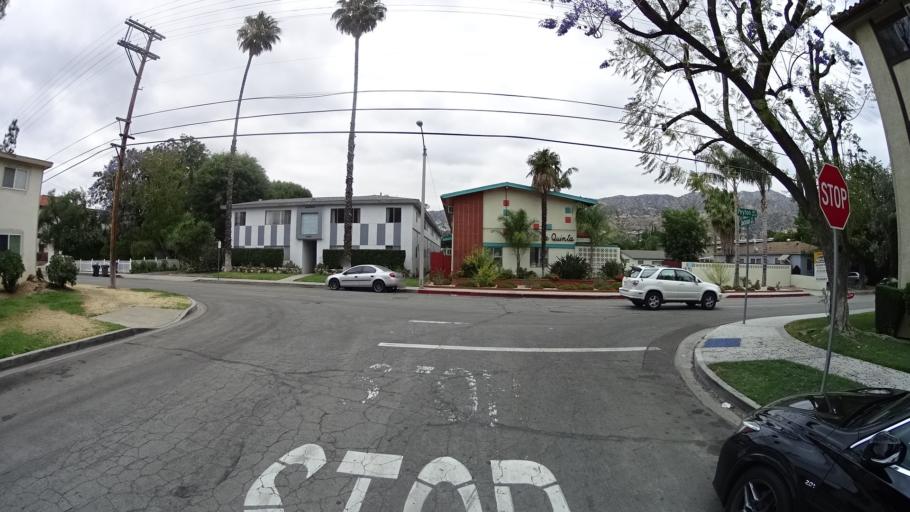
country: US
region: California
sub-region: Los Angeles County
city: Burbank
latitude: 34.1963
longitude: -118.3296
